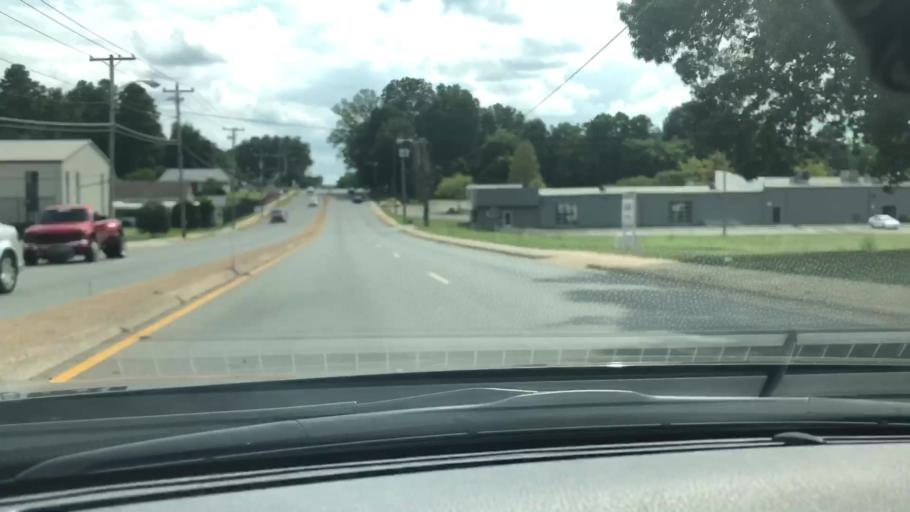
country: US
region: North Carolina
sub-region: Mecklenburg County
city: Charlotte
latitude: 35.1944
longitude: -80.8784
